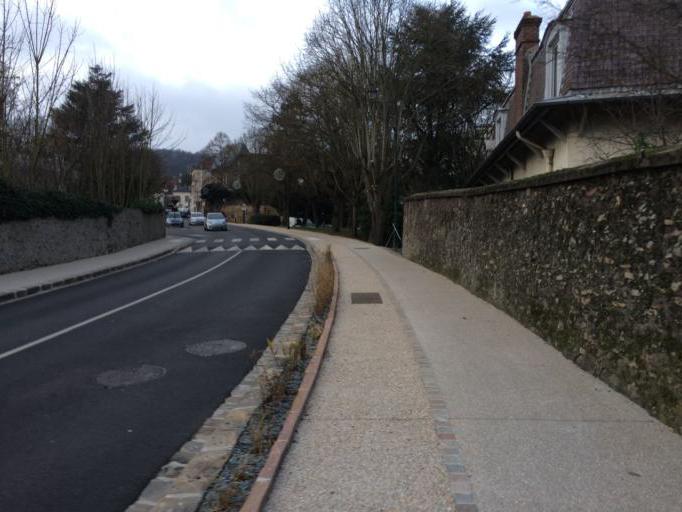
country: FR
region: Ile-de-France
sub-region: Departement de l'Essonne
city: Bievres
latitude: 48.7536
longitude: 2.2159
